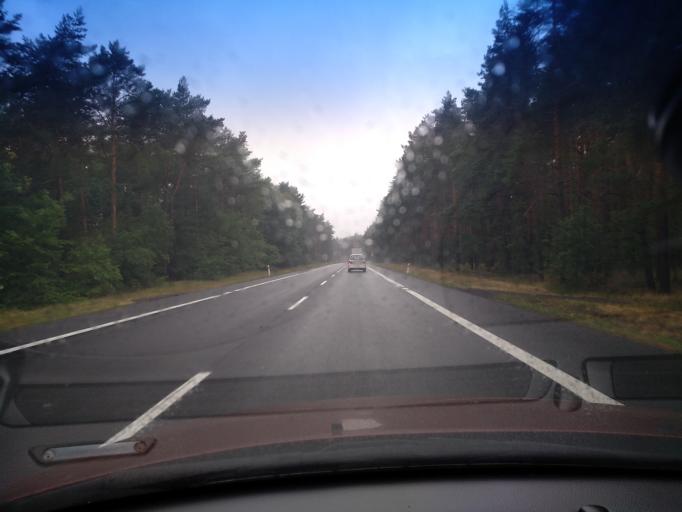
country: PL
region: Lower Silesian Voivodeship
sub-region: Powiat zgorzelecki
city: Wegliniec
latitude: 51.2204
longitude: 15.2244
